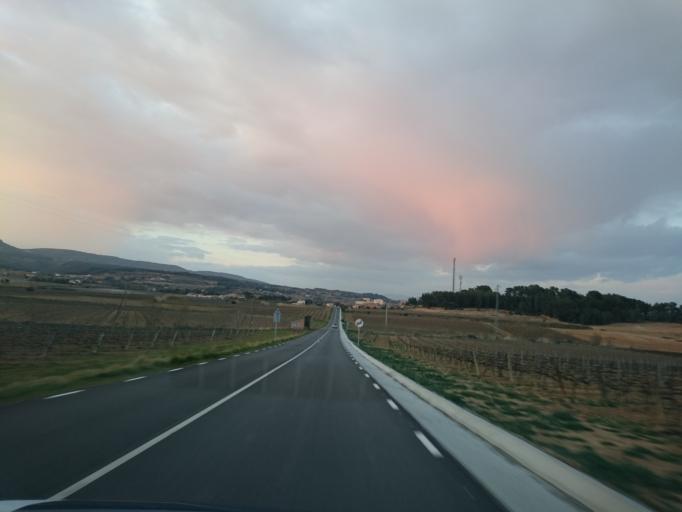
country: ES
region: Catalonia
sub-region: Provincia de Barcelona
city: Sant Marti Sarroca
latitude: 41.3845
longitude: 1.5939
